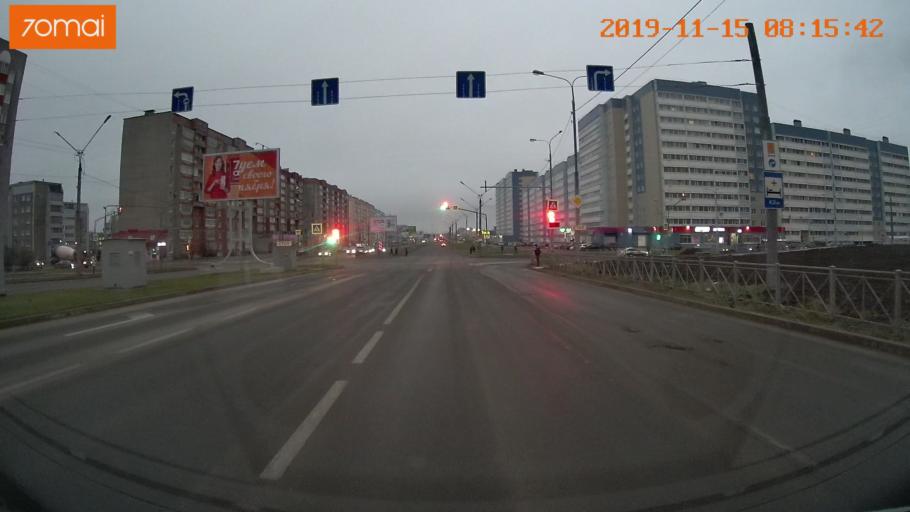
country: RU
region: Vologda
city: Cherepovets
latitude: 59.0842
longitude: 37.9210
